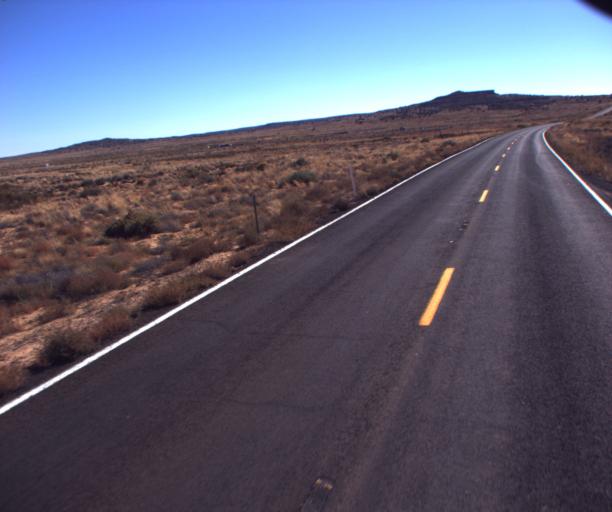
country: US
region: Arizona
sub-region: Navajo County
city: First Mesa
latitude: 35.9746
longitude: -110.6981
